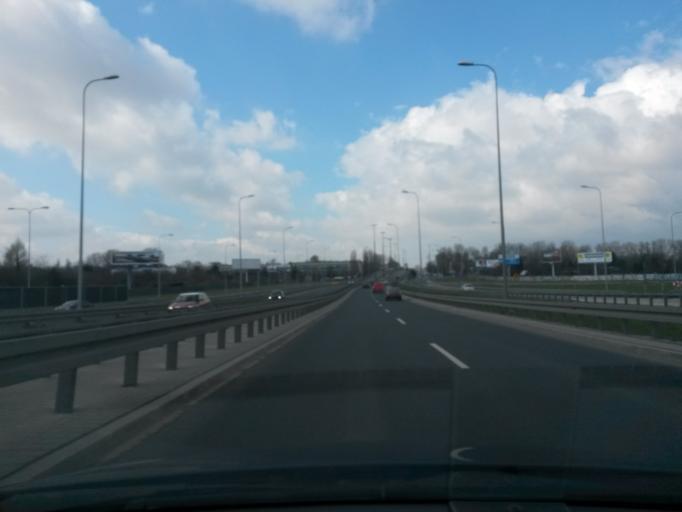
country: PL
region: Masovian Voivodeship
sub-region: Warszawa
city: Wlochy
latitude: 52.1821
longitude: 20.9846
